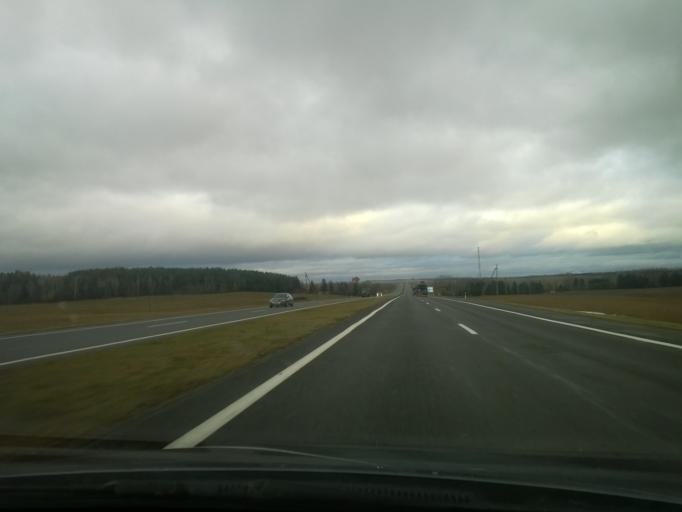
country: BY
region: Minsk
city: Snow
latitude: 53.2918
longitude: 26.3469
